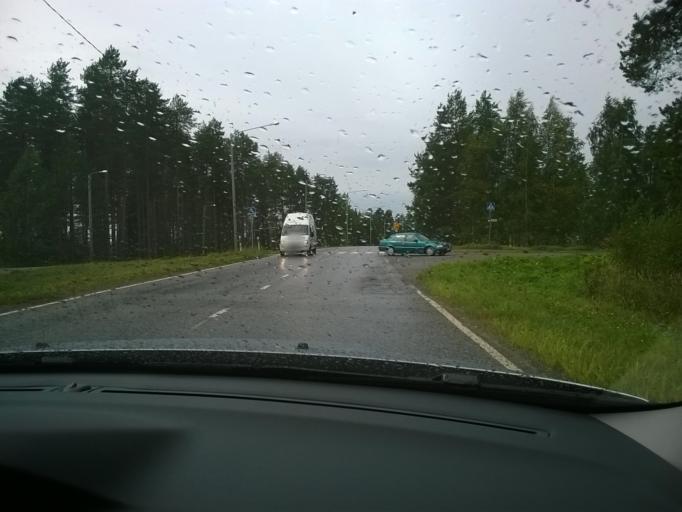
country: FI
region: Kainuu
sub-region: Kehys-Kainuu
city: Kuhmo
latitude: 64.1208
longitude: 29.5463
